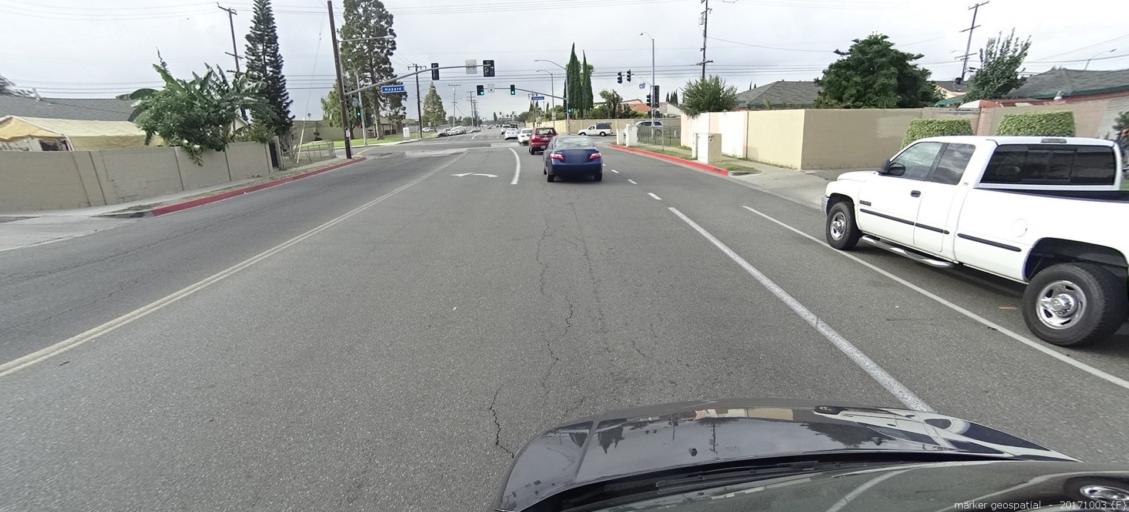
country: US
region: California
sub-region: Orange County
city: Garden Grove
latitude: 33.7529
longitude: -117.9461
